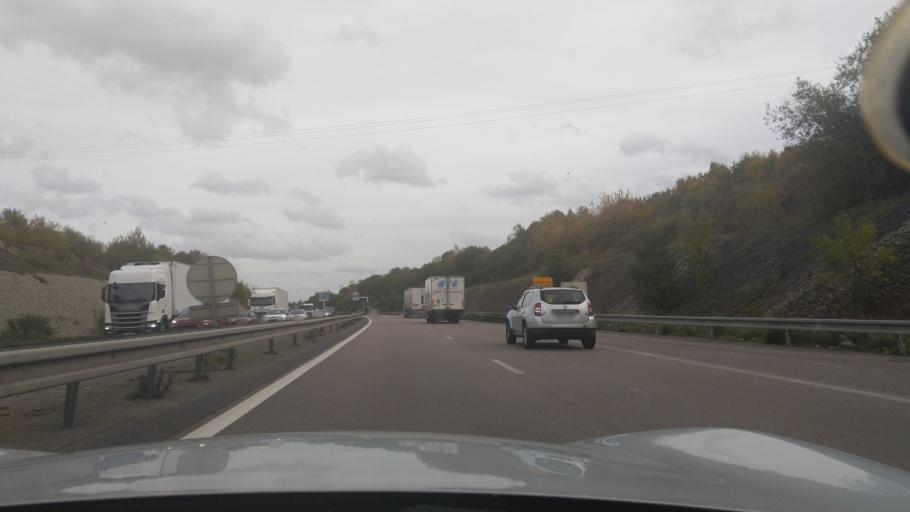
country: FR
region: Ile-de-France
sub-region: Departement du Val-d'Oise
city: Louvres
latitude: 49.0329
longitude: 2.4901
